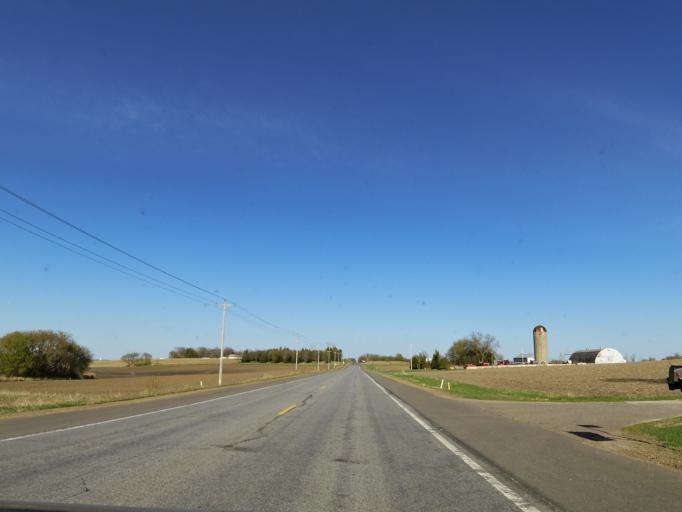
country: US
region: Minnesota
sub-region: Dakota County
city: Lakeville
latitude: 44.6235
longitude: -93.2835
